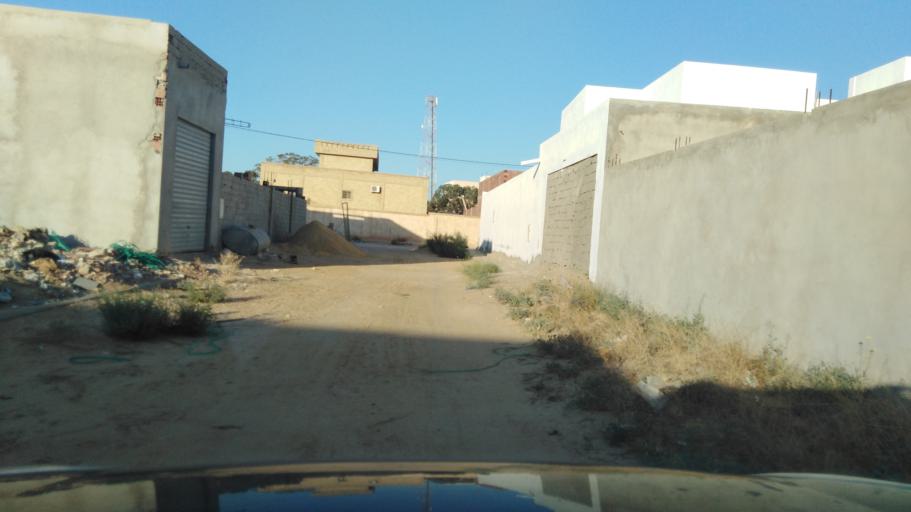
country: TN
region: Qabis
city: Gabes
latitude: 33.9513
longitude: 10.0150
